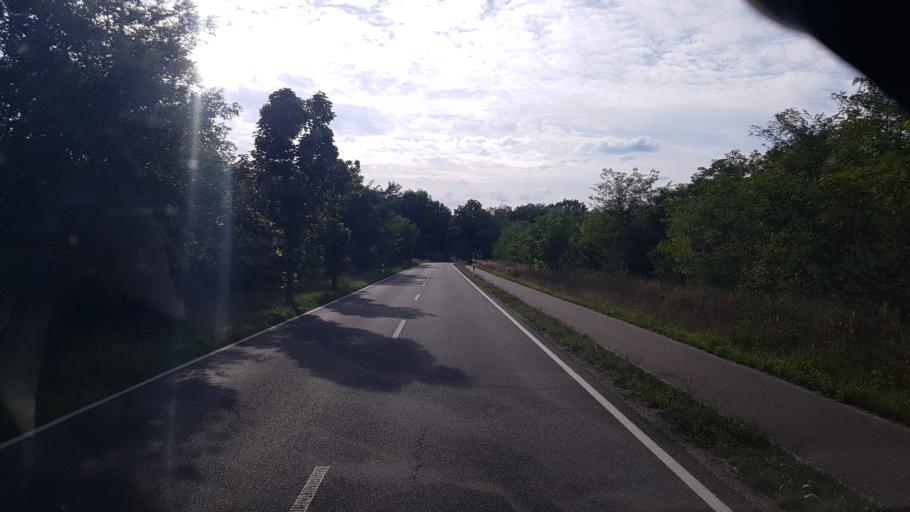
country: DE
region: Brandenburg
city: Welzow
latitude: 51.5506
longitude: 14.2192
